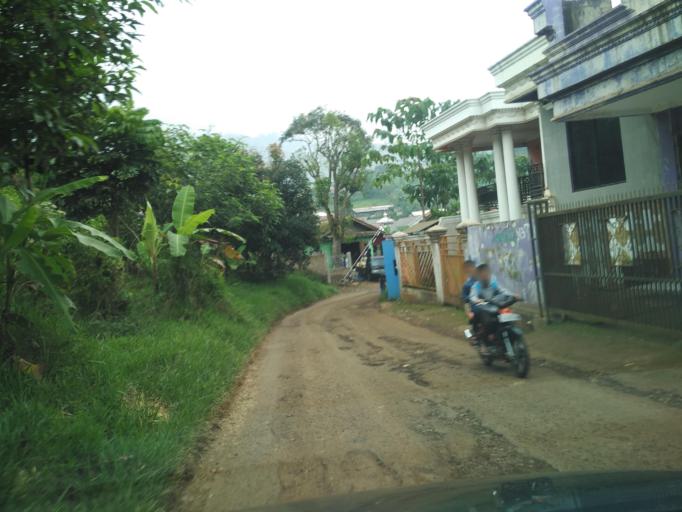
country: ID
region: West Java
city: Caringin
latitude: -6.6847
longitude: 107.0308
